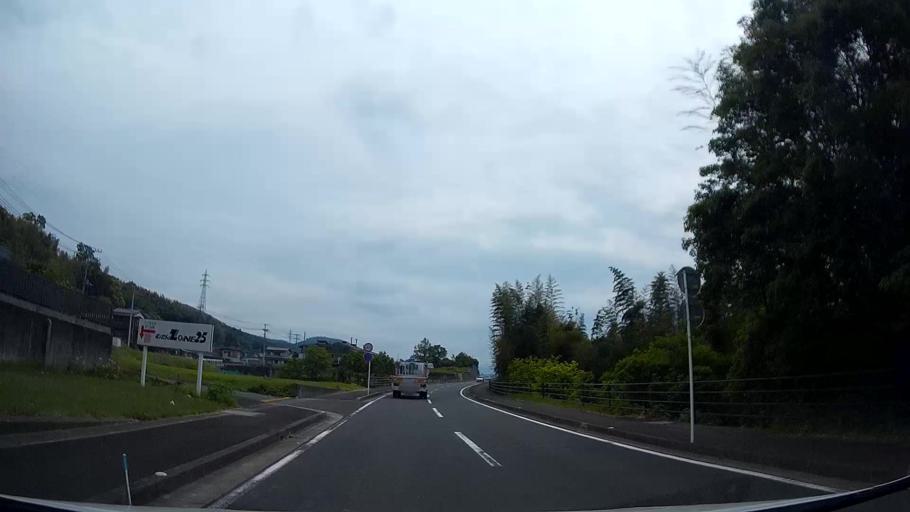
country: JP
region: Shizuoka
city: Ito
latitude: 34.9668
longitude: 138.9471
